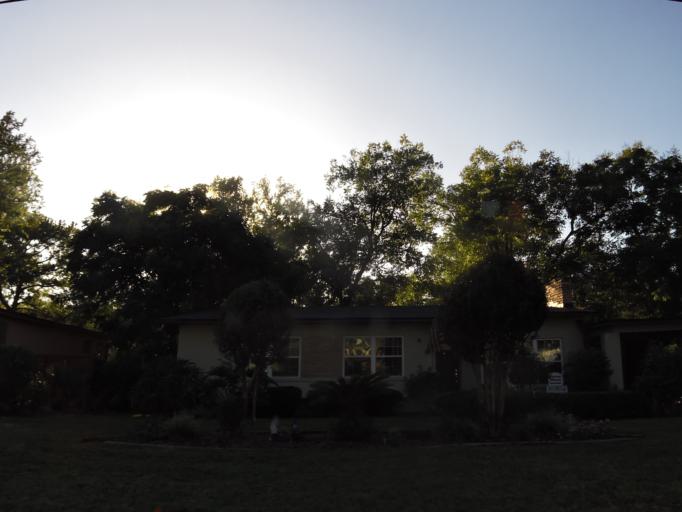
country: US
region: Florida
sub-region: Duval County
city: Jacksonville
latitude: 30.2670
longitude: -81.6434
